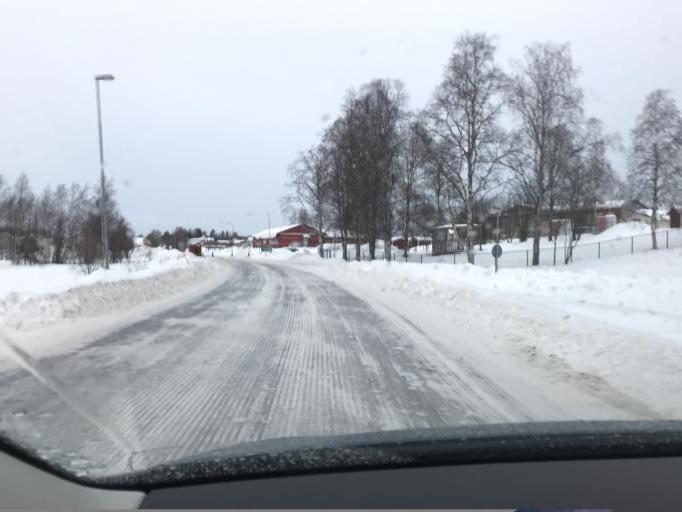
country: SE
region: Norrbotten
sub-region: Lulea Kommun
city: Sodra Sunderbyn
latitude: 65.6626
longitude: 21.9297
